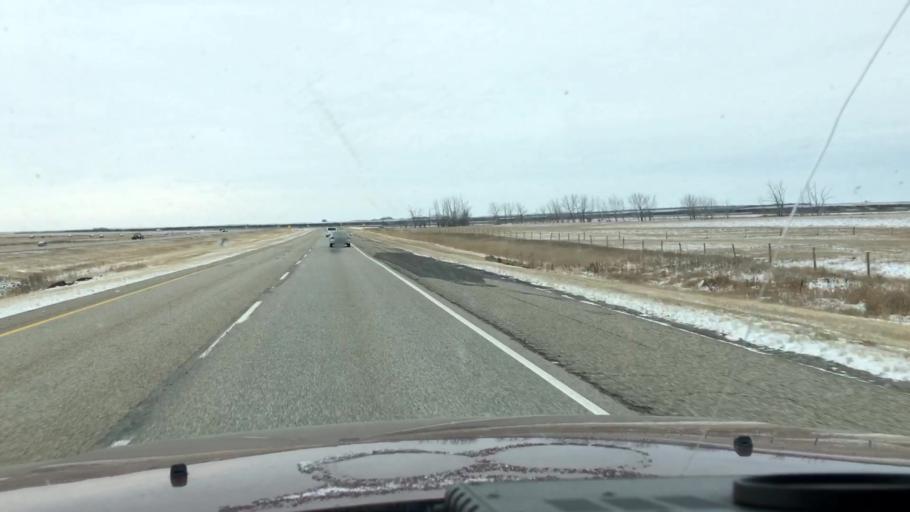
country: CA
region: Saskatchewan
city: Saskatoon
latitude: 51.4807
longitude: -106.2503
